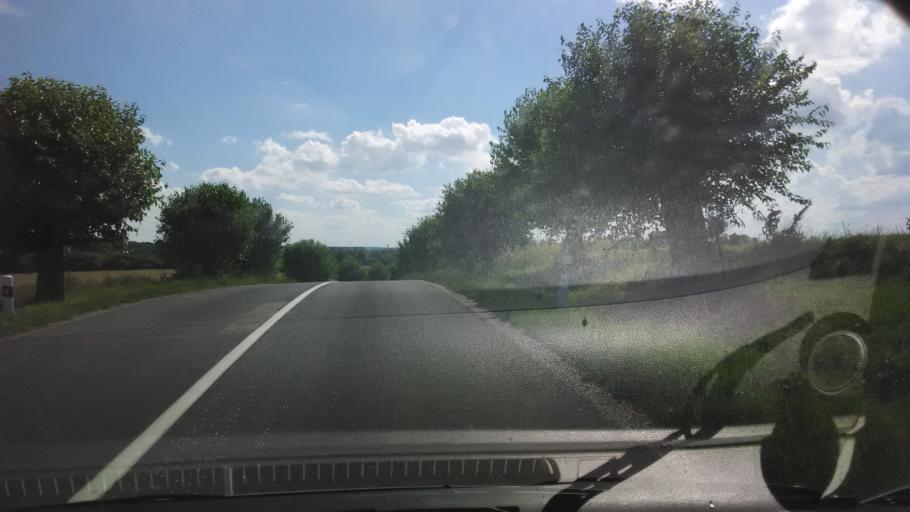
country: SK
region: Nitriansky
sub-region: Okres Nitra
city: Vrable
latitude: 48.1521
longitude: 18.4253
